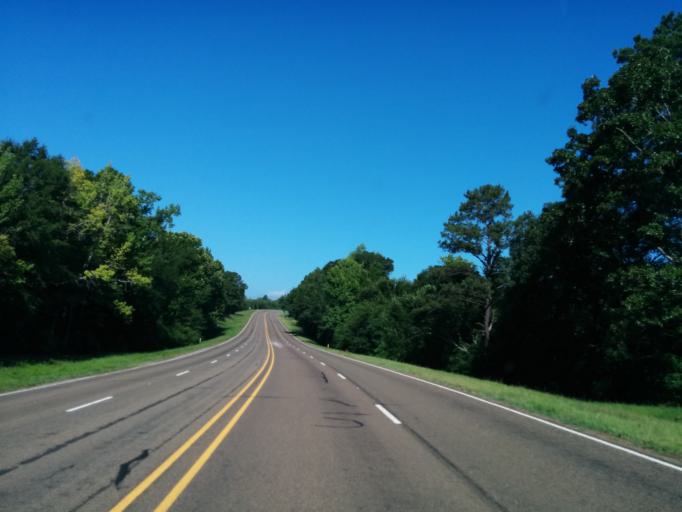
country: US
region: Texas
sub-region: Sabine County
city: Milam
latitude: 31.4314
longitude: -93.8197
